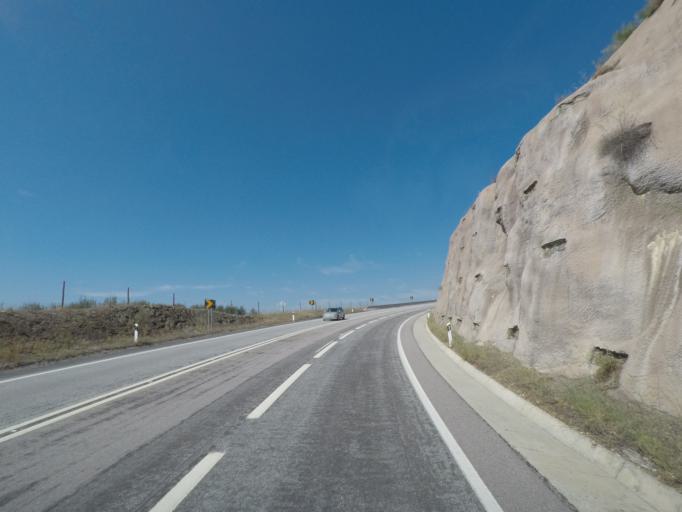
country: PT
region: Braganca
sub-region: Alfandega da Fe
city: Alfandega da Fe
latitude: 41.2764
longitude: -6.8923
